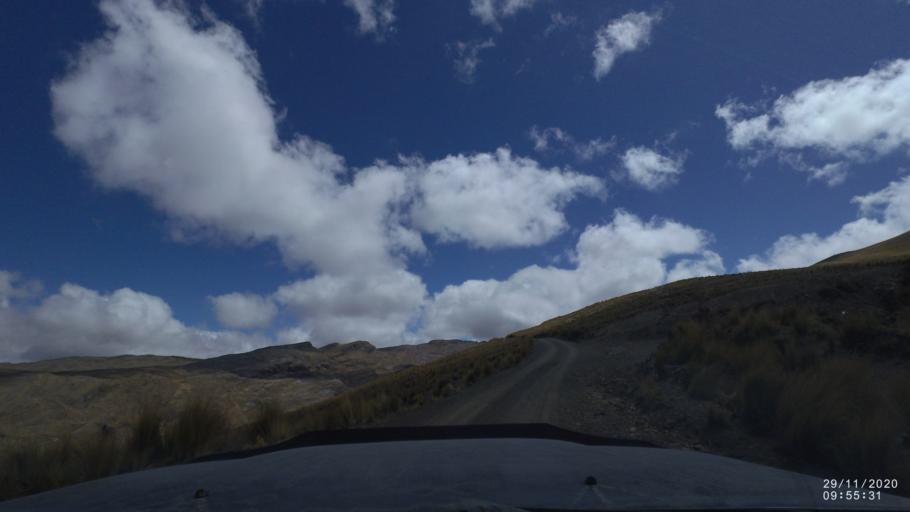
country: BO
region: Cochabamba
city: Cochabamba
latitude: -17.2746
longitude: -66.1784
